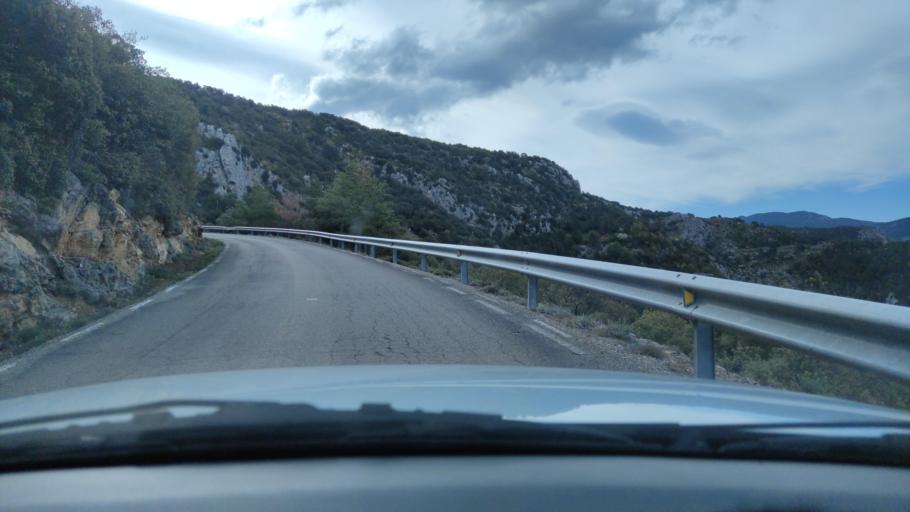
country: ES
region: Catalonia
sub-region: Provincia de Lleida
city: Coll de Nargo
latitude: 42.2488
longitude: 1.3641
